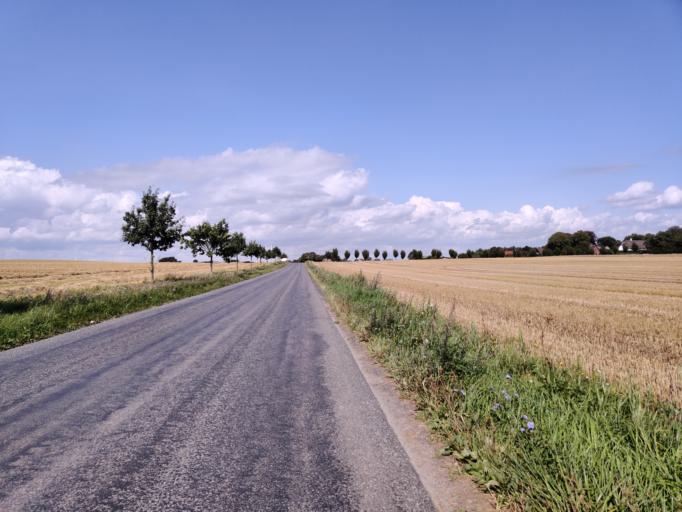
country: DK
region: Zealand
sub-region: Guldborgsund Kommune
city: Nykobing Falster
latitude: 54.6501
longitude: 11.8876
